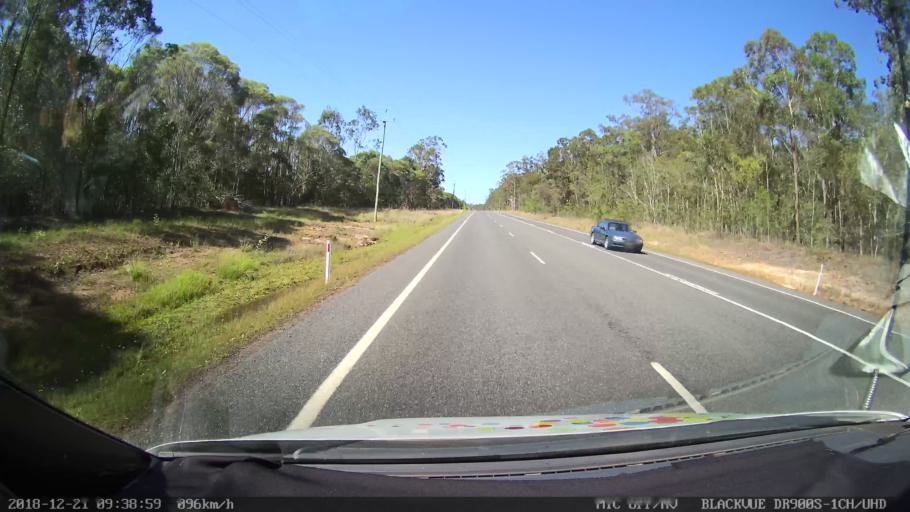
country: AU
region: New South Wales
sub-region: Clarence Valley
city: Grafton
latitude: -29.5560
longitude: 152.9777
